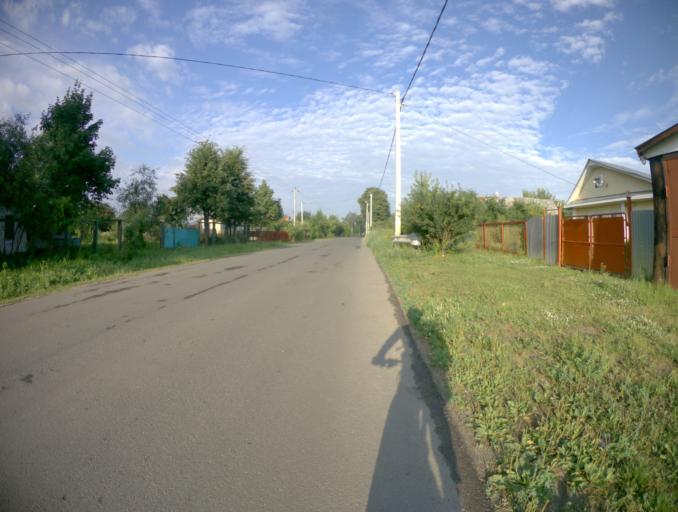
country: RU
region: Vladimir
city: Galitsy
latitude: 56.1610
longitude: 42.8191
